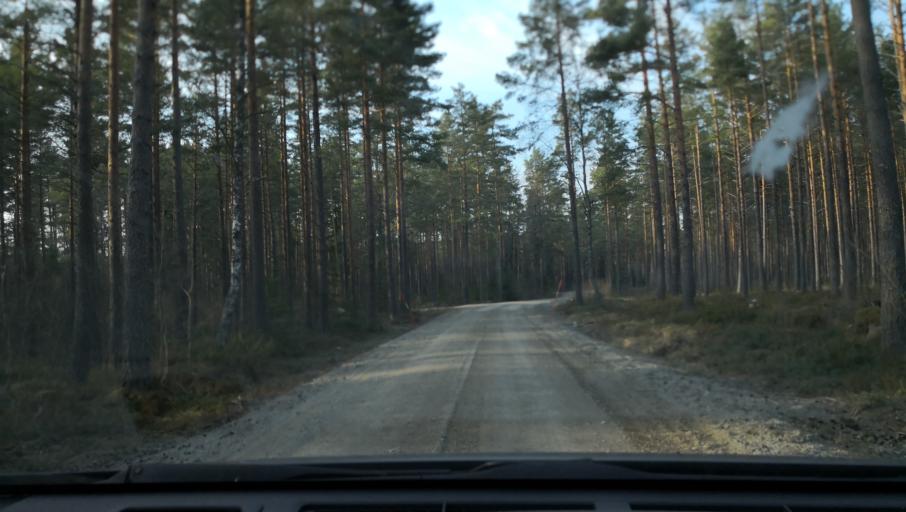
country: SE
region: OErebro
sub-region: Orebro Kommun
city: Hovsta
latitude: 59.3602
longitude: 15.3285
